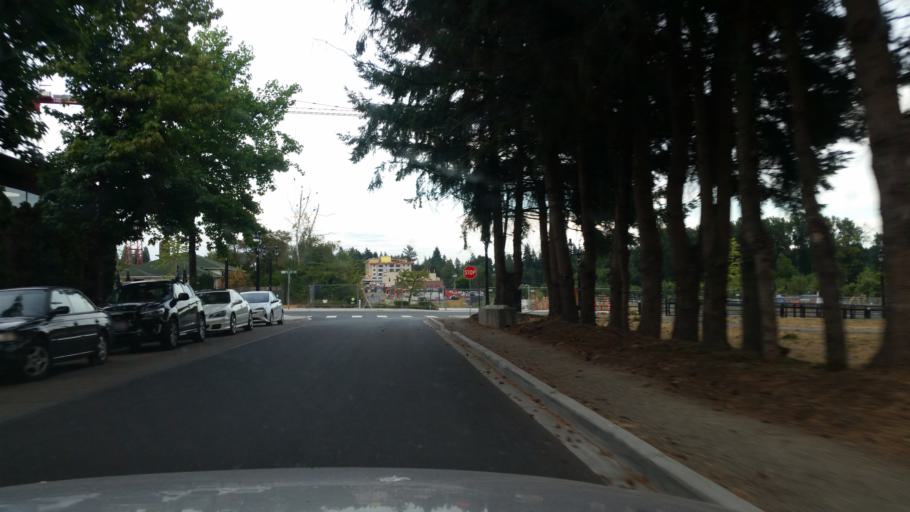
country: US
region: Washington
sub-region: King County
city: Bothell
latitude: 47.7600
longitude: -122.2105
